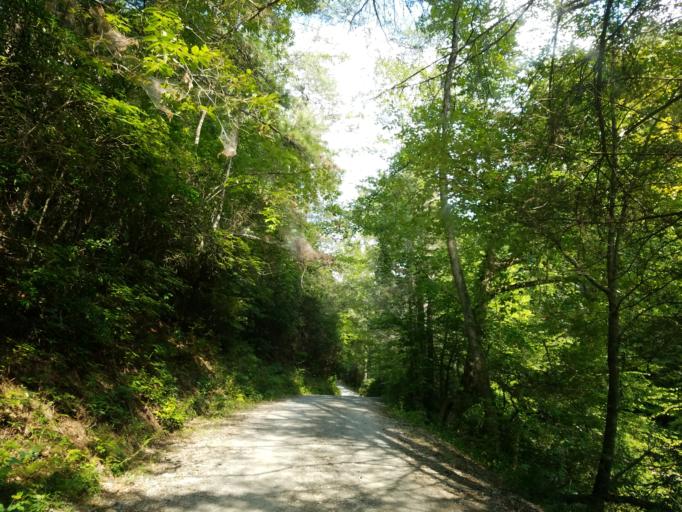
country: US
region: Georgia
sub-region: Fannin County
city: Blue Ridge
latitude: 34.7880
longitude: -84.4098
